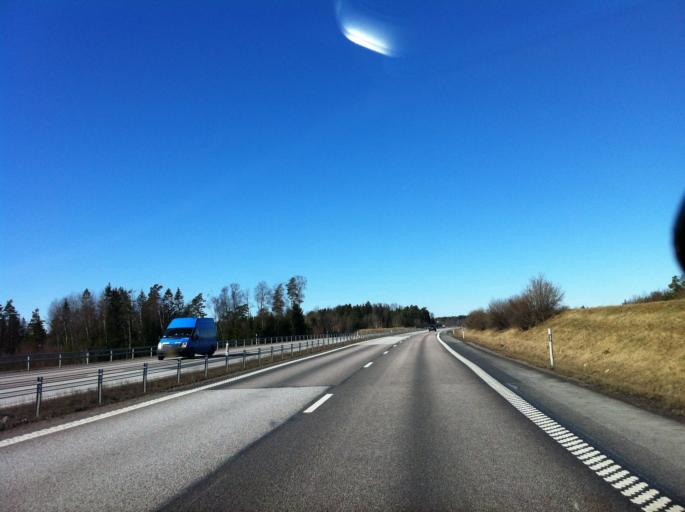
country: SE
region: Vaestra Goetaland
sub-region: Vanersborgs Kommun
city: Vanersborg
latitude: 58.3695
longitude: 12.3495
